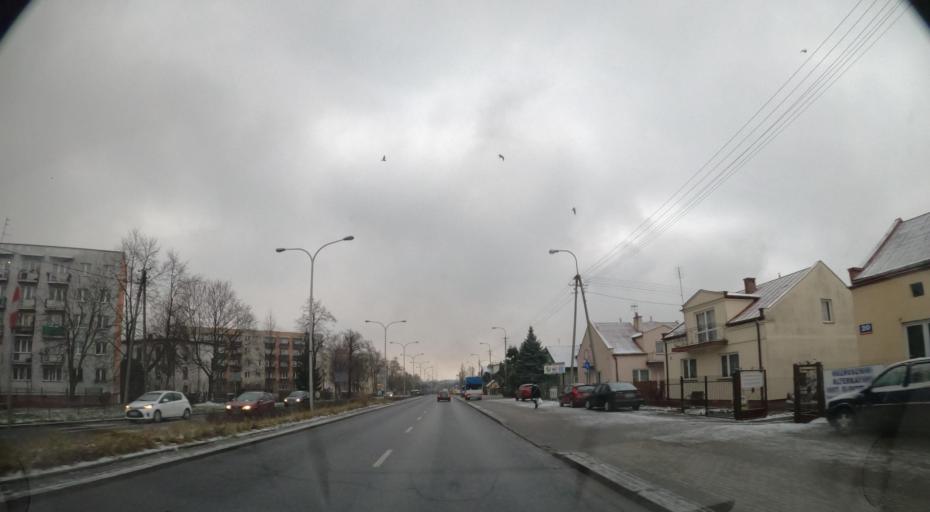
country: PL
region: Masovian Voivodeship
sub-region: Plock
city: Plock
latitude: 52.5554
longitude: 19.6703
